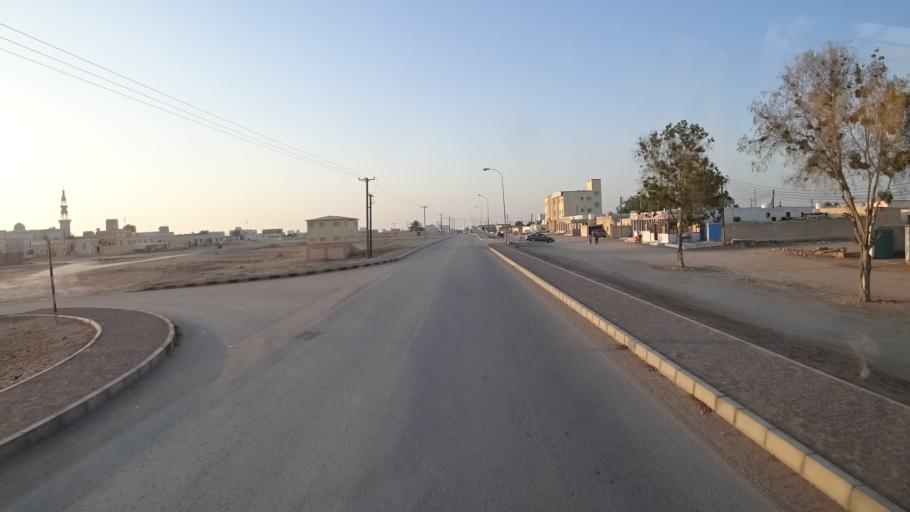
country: OM
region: Ash Sharqiyah
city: Sur
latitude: 22.5219
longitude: 59.7923
